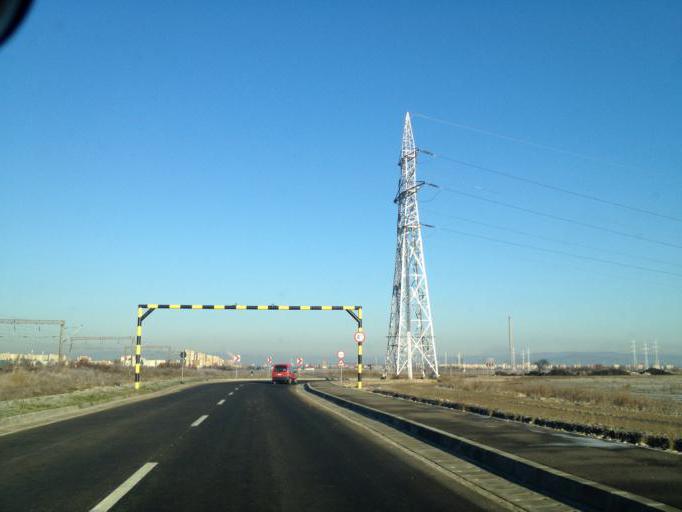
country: RO
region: Brasov
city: Brasov
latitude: 45.6295
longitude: 25.6478
